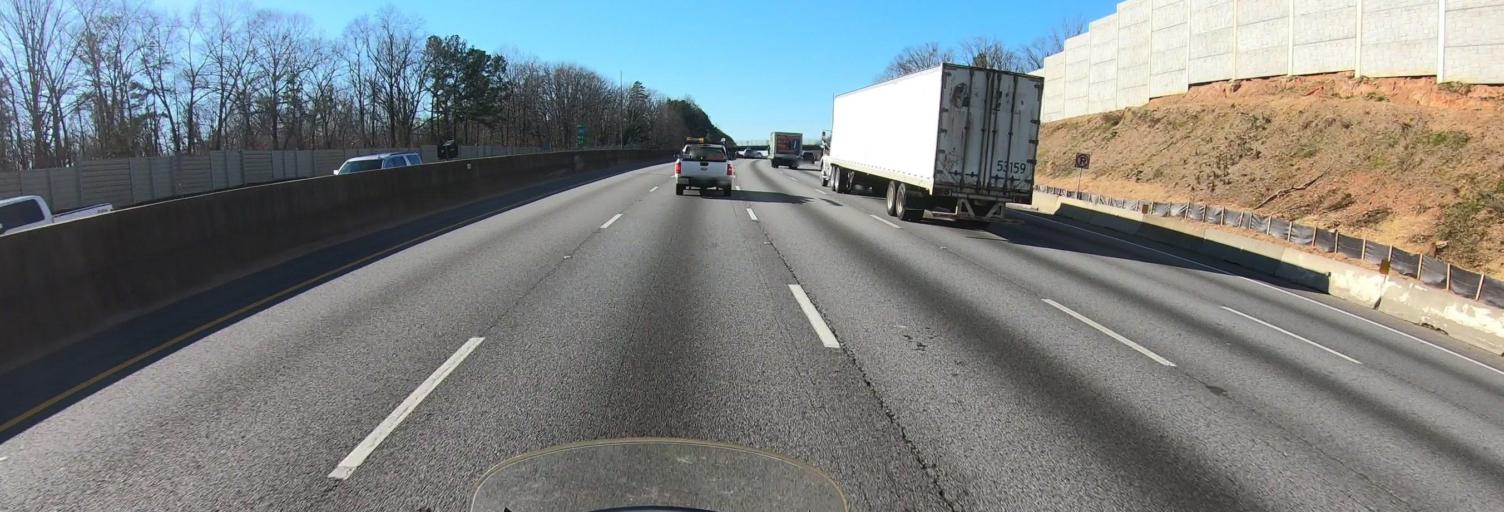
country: US
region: Georgia
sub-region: Fulton County
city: Sandy Springs
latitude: 33.9128
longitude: -84.3969
